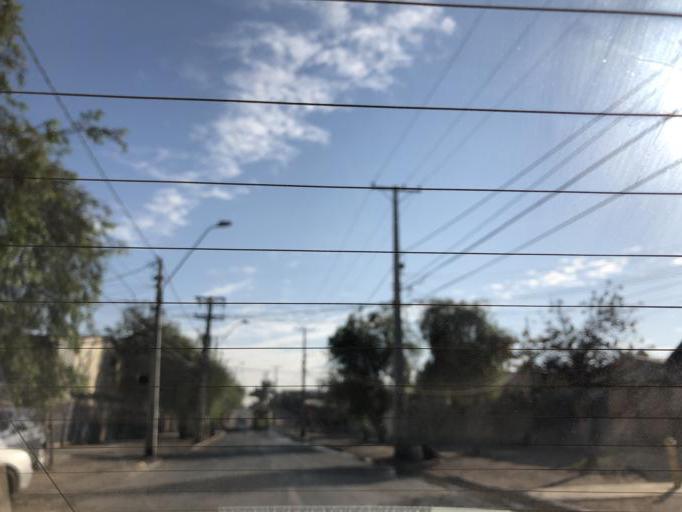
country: CL
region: Santiago Metropolitan
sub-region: Provincia de Cordillera
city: Puente Alto
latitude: -33.6265
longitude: -70.5937
